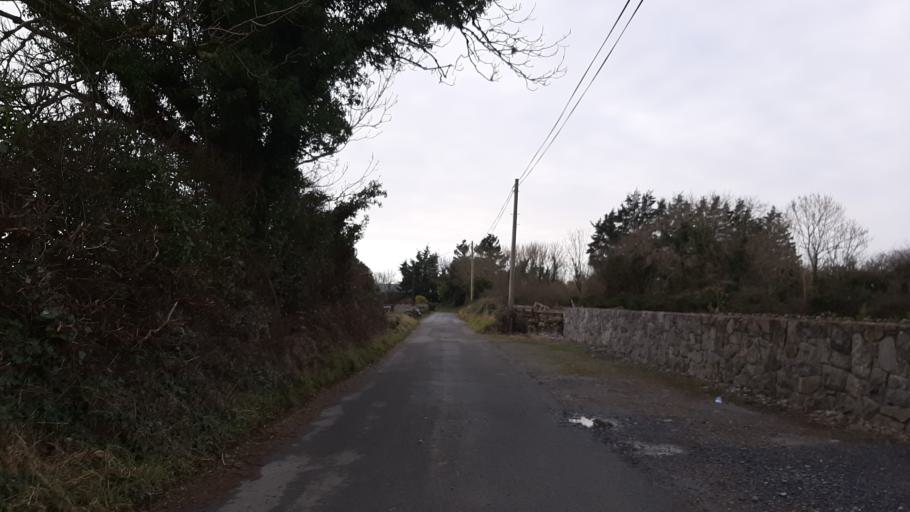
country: IE
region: Connaught
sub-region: County Galway
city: Gaillimh
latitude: 53.3062
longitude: -9.0708
